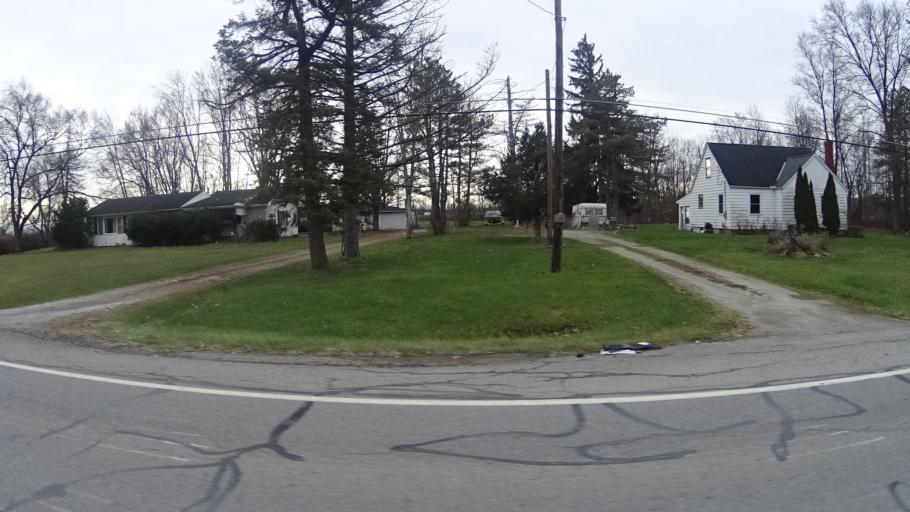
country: US
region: Ohio
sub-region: Lorain County
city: Wellington
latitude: 41.1690
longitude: -82.2412
